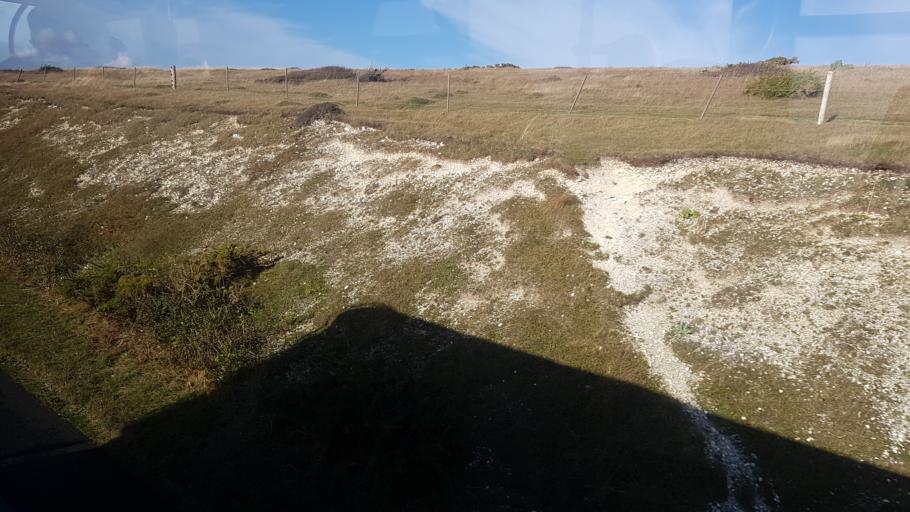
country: GB
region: England
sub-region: Isle of Wight
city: Freshwater
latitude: 50.6693
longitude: -1.4941
